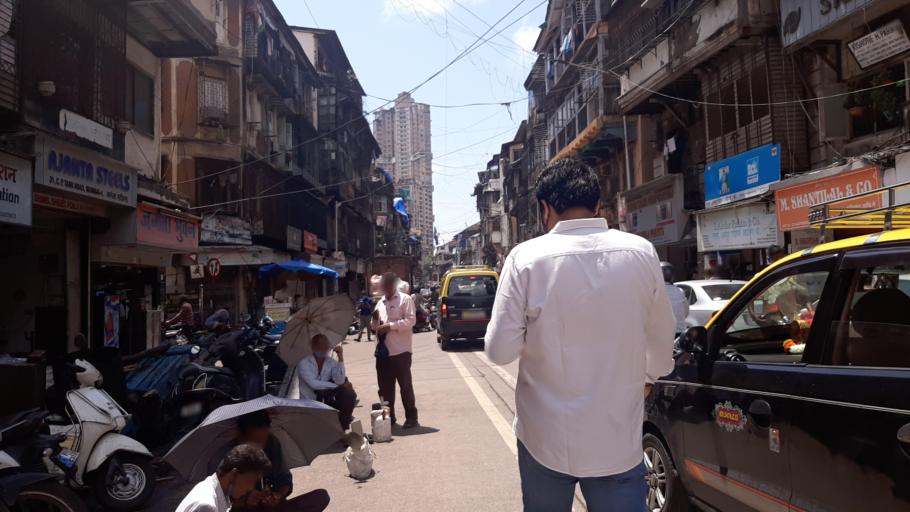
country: IN
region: Maharashtra
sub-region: Mumbai Suburban
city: Mumbai
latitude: 18.9564
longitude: 72.8282
